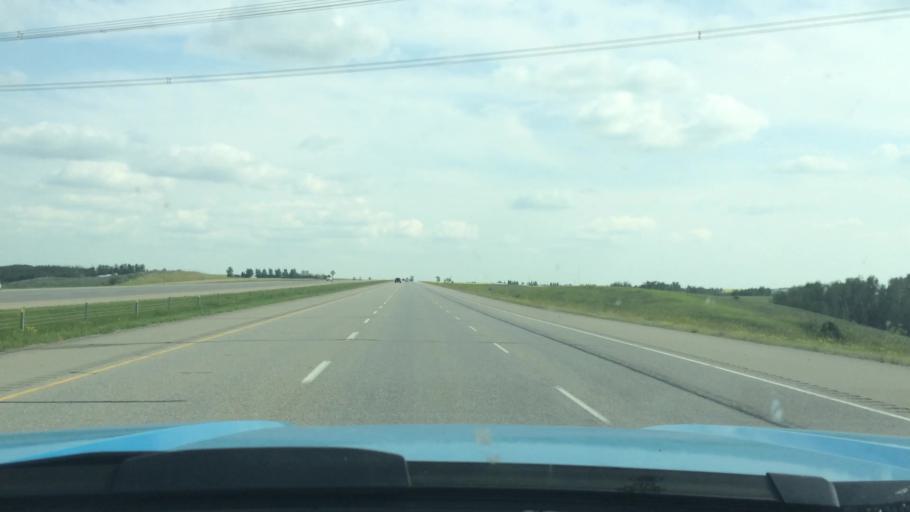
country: CA
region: Alberta
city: Crossfield
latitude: 51.4609
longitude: -114.0237
